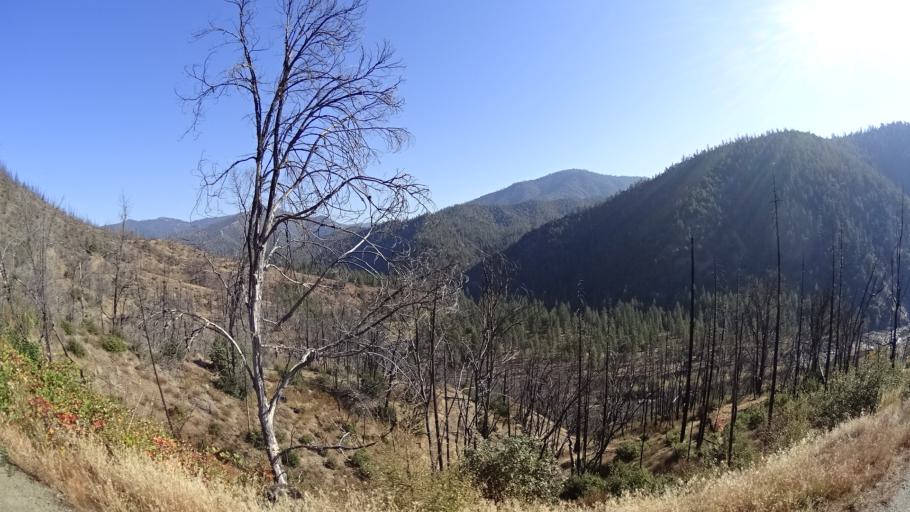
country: US
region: California
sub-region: Siskiyou County
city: Happy Camp
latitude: 41.7213
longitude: -123.0198
